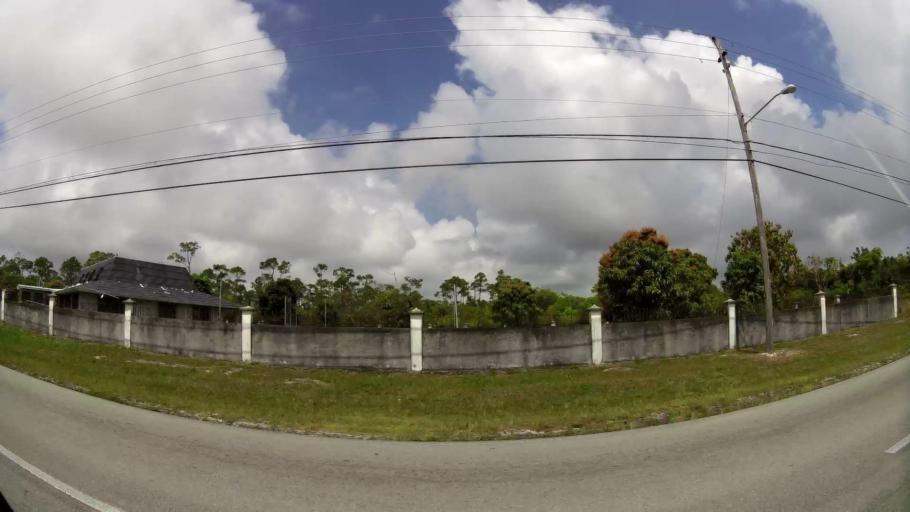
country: BS
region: Freeport
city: Lucaya
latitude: 26.5295
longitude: -78.6195
